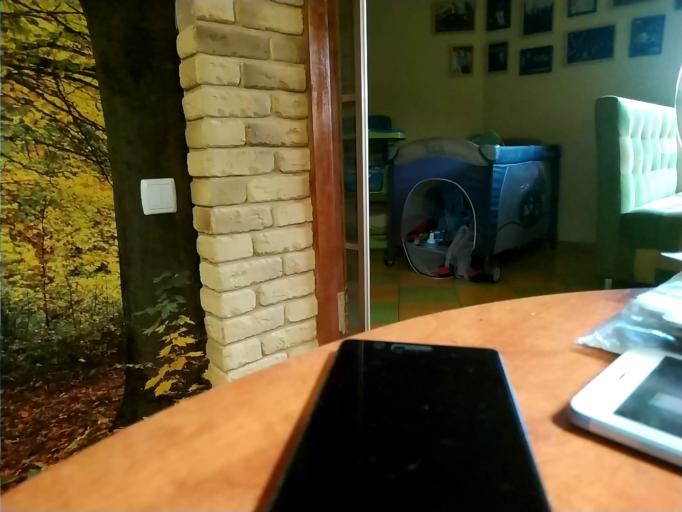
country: RU
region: Kaluga
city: Khvastovichi
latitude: 53.6595
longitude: 35.4468
